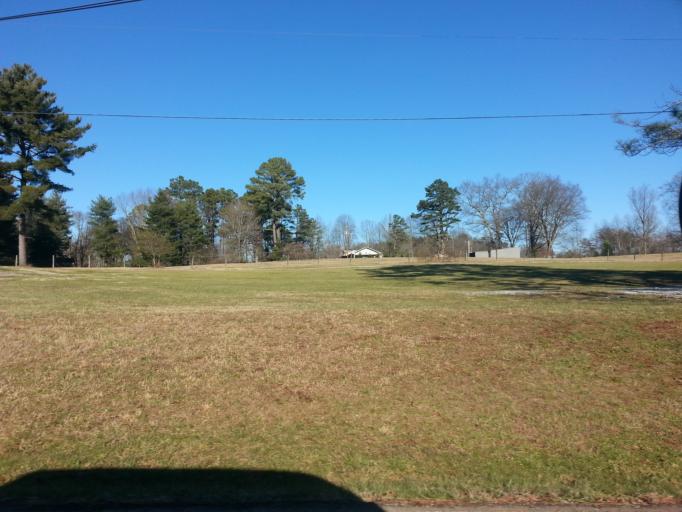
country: US
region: Tennessee
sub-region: Blount County
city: Louisville
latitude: 35.8973
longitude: -84.0031
